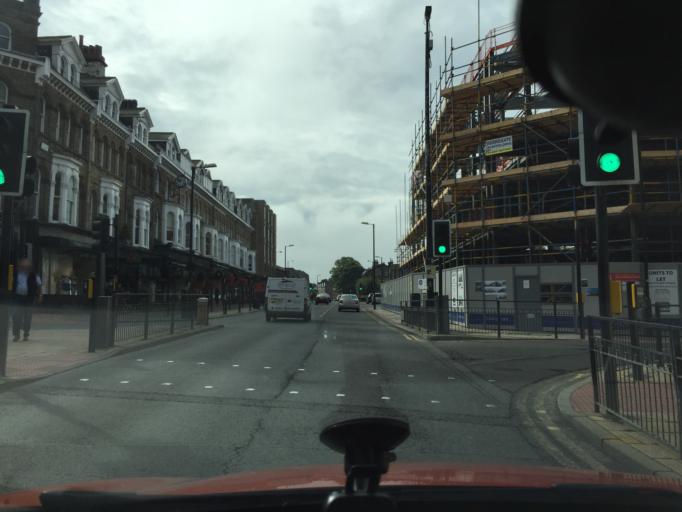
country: GB
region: England
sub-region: North Yorkshire
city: Harrogate
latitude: 53.9920
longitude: -1.5378
